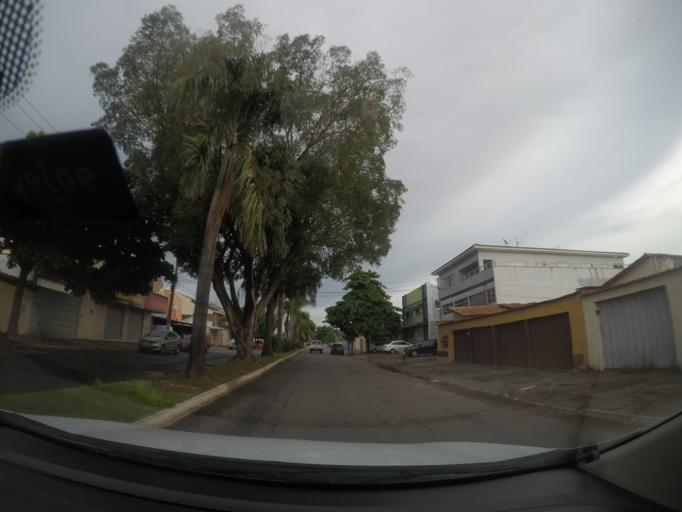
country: BR
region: Goias
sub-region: Goiania
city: Goiania
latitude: -16.7134
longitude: -49.3108
